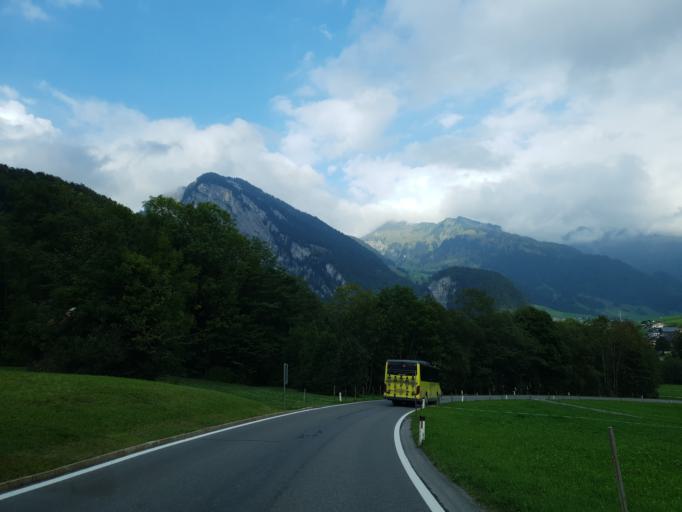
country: AT
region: Vorarlberg
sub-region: Politischer Bezirk Bregenz
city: Au
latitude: 47.3184
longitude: 9.9592
